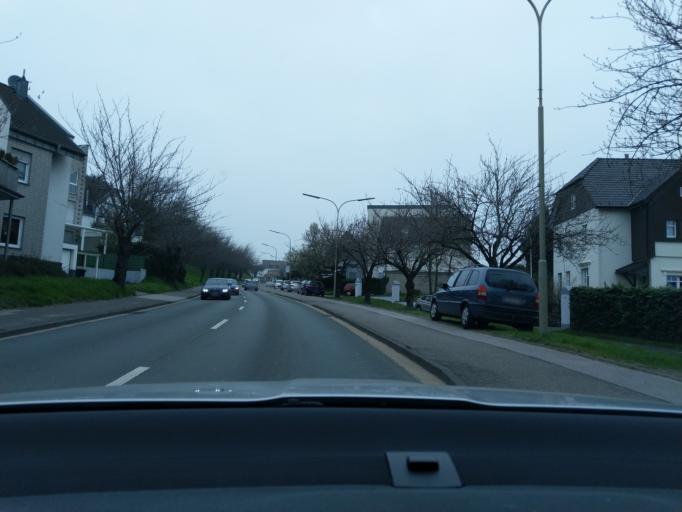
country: DE
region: North Rhine-Westphalia
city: Huckelhoven
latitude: 51.0570
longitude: 6.2297
